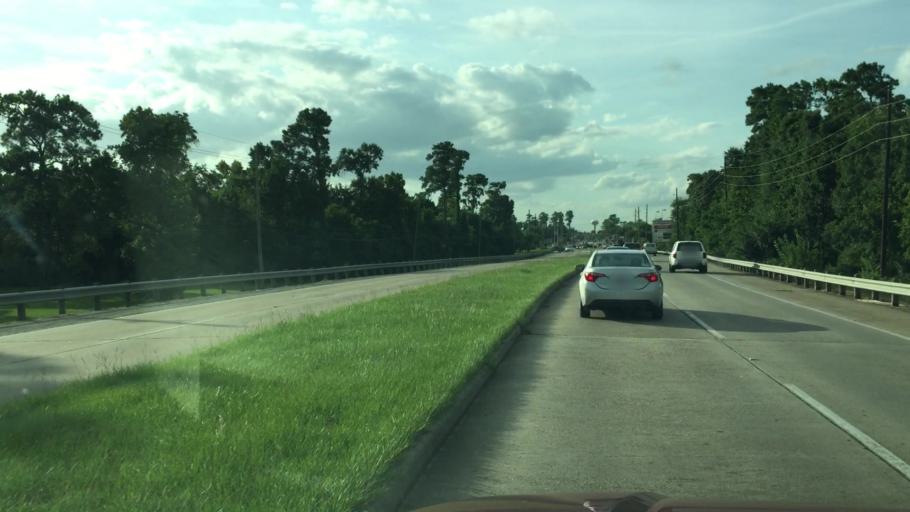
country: US
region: Texas
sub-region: Harris County
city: Hudson
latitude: 30.0073
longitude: -95.5125
